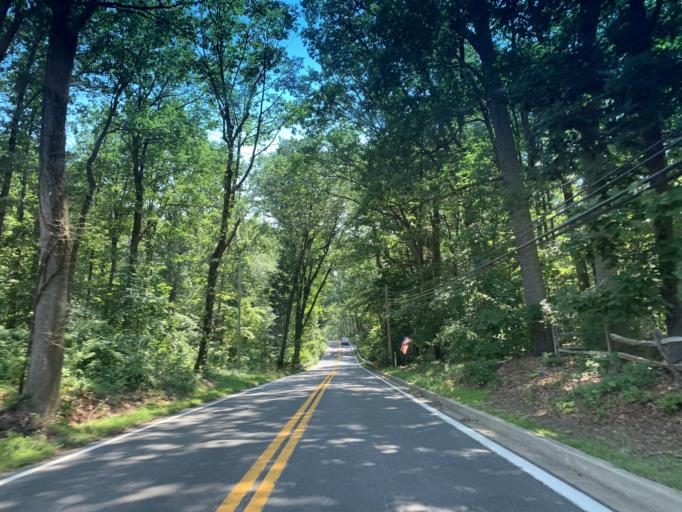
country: US
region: Maryland
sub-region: Montgomery County
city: Clarksburg
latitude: 39.2322
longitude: -77.3642
